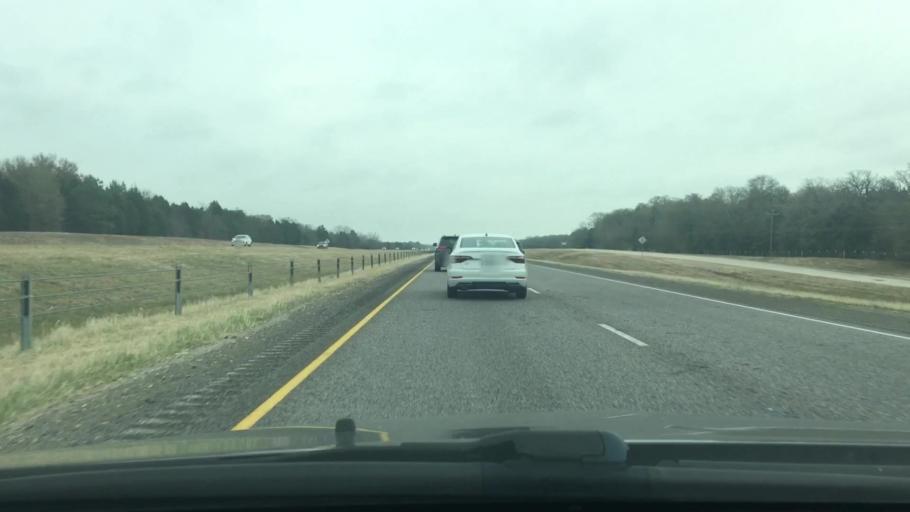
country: US
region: Texas
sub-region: Freestone County
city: Fairfield
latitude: 31.7485
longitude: -96.1982
